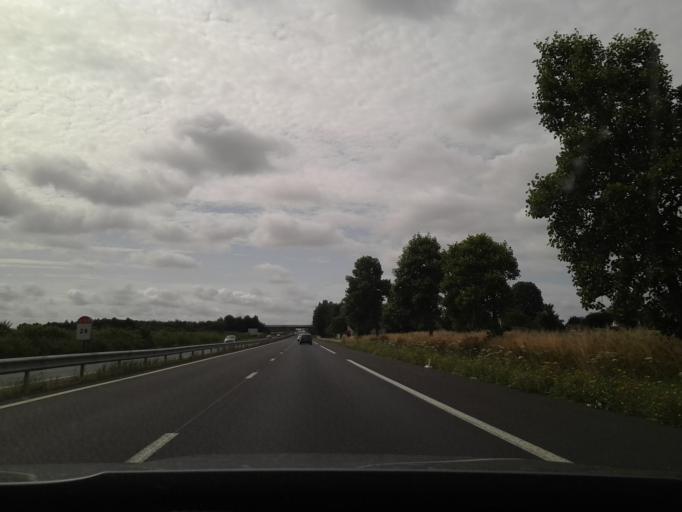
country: FR
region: Lower Normandy
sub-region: Departement du Calvados
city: Bretteville-sur-Laize
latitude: 49.0596
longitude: -0.2895
